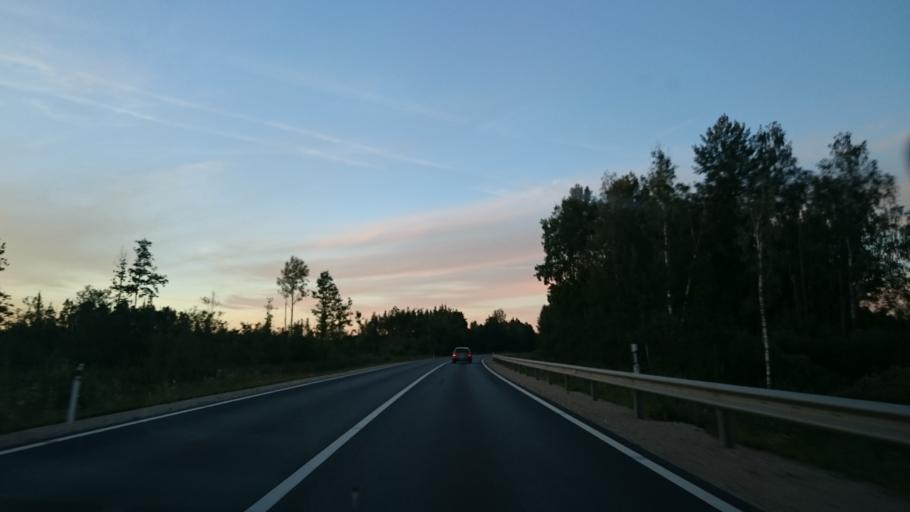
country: LV
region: Dobeles Rajons
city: Dobele
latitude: 56.7176
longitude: 23.1923
